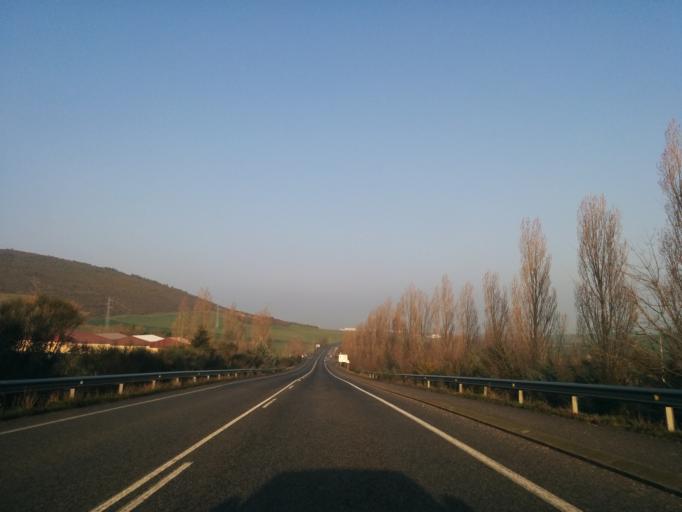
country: ES
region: Navarre
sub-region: Provincia de Navarra
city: Elorz
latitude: 42.7664
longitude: -1.5849
